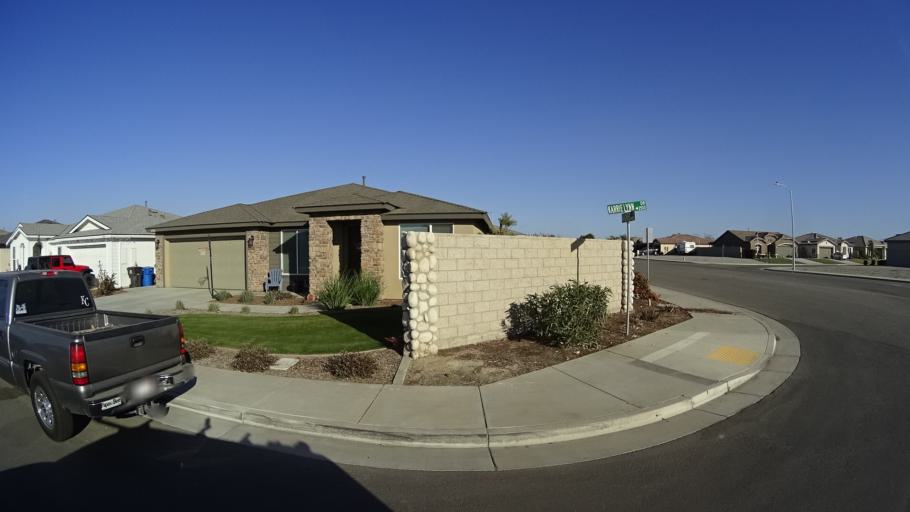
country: US
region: California
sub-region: Kern County
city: Greenfield
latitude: 35.2711
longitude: -119.0303
